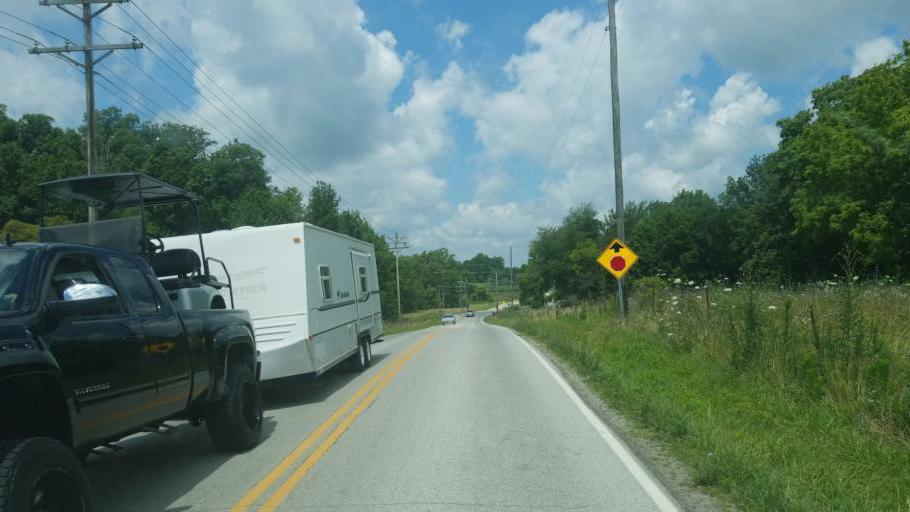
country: US
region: Ohio
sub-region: Highland County
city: Leesburg
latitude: 39.2511
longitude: -83.4711
